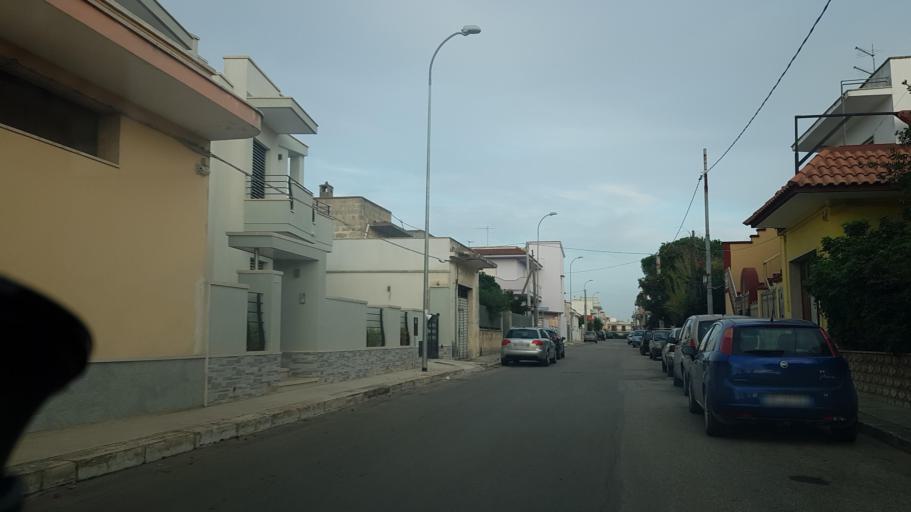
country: IT
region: Apulia
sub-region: Provincia di Brindisi
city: San Pancrazio Salentino
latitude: 40.4190
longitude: 17.8294
